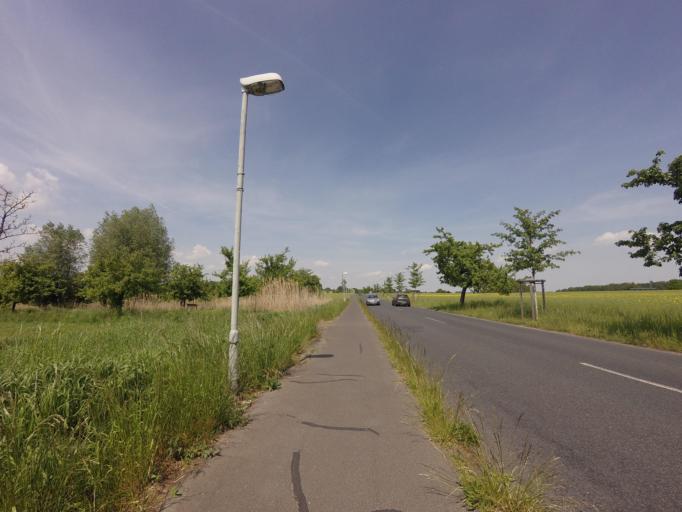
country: DE
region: Lower Saxony
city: Cremlingen
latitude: 52.2826
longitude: 10.6043
